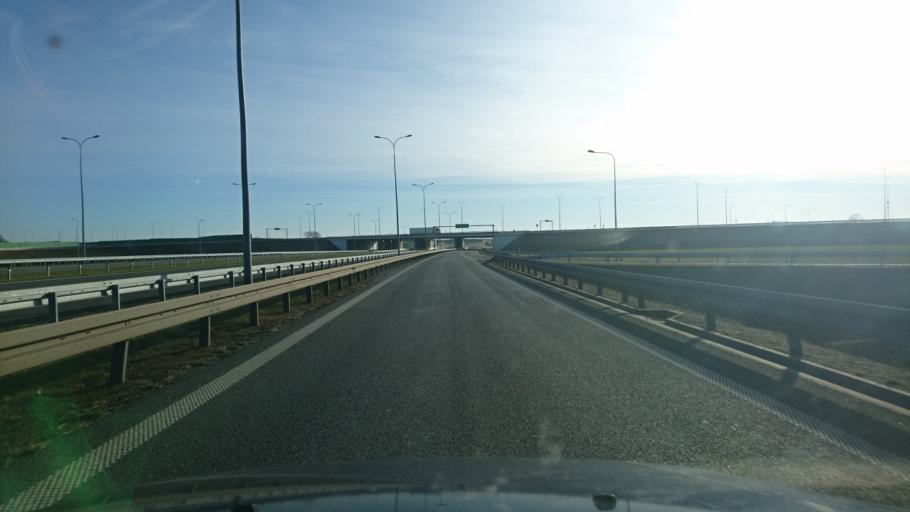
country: PL
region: Greater Poland Voivodeship
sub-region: Powiat kepinski
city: Kepno
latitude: 51.3179
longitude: 18.0071
